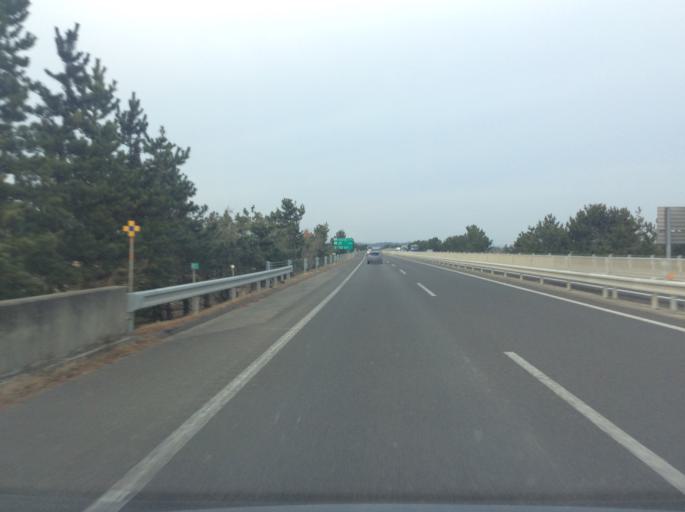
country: JP
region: Miyagi
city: Iwanuma
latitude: 38.1125
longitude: 140.8887
